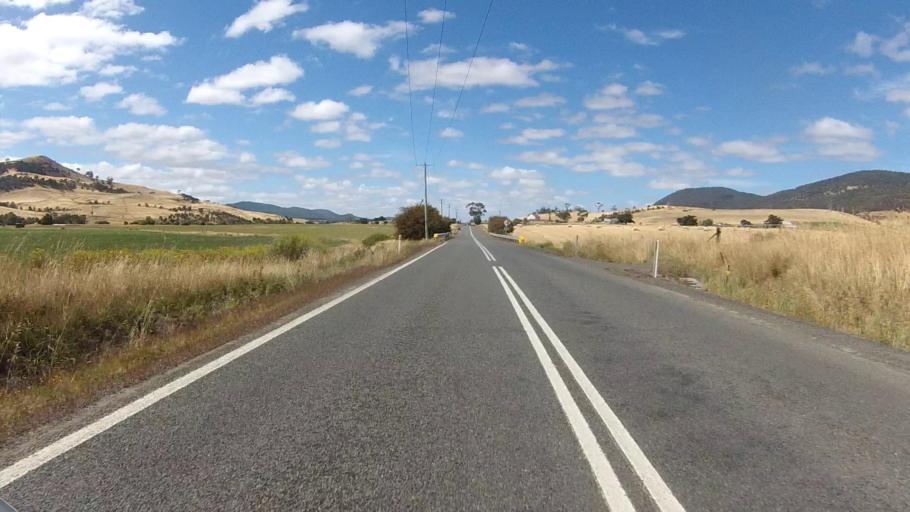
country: AU
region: Tasmania
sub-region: Brighton
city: Bridgewater
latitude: -42.5880
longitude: 147.4084
